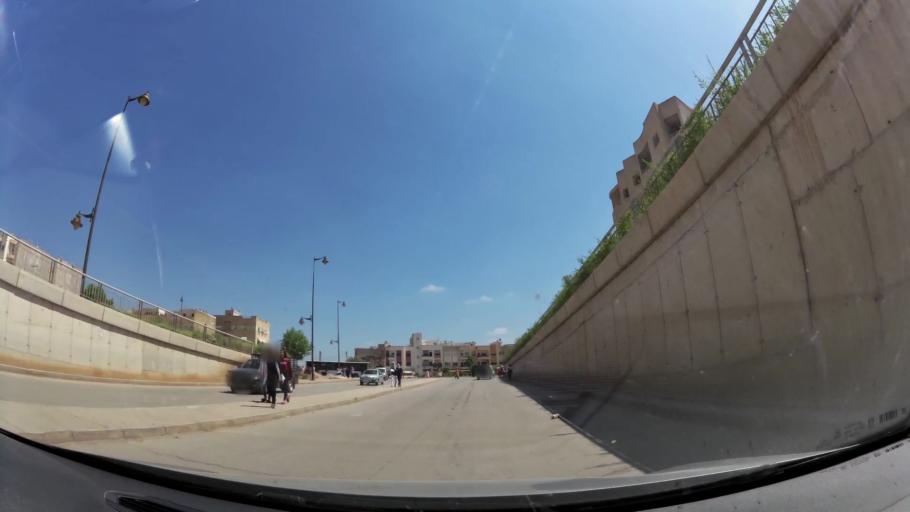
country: MA
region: Fes-Boulemane
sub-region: Fes
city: Fes
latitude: 34.0217
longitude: -5.0394
